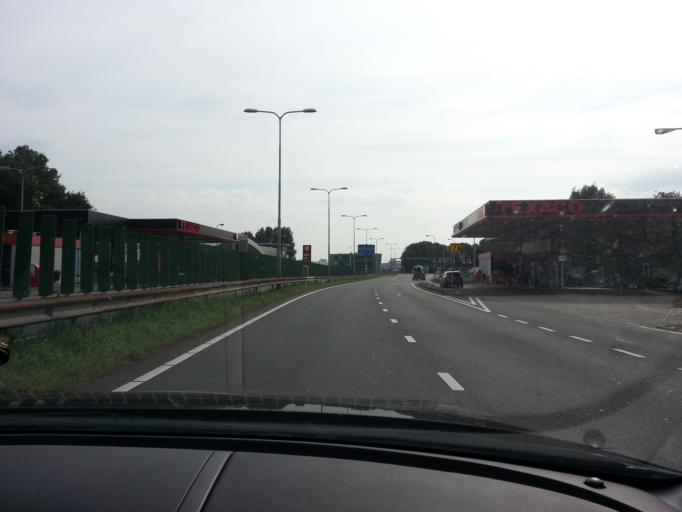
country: NL
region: South Holland
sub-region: Gemeente Spijkenisse
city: Spijkenisse
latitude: 51.8583
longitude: 4.3050
